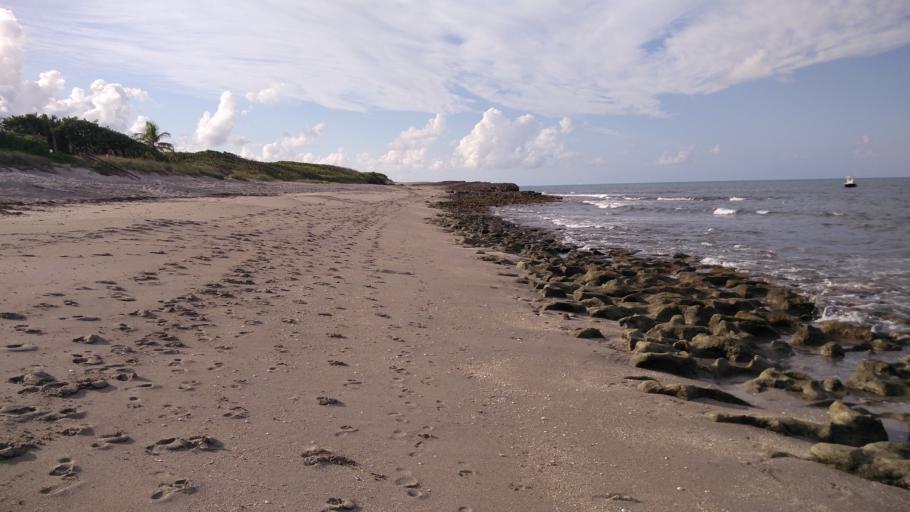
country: US
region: Florida
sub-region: Palm Beach County
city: Jupiter
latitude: 26.9722
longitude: -80.0808
